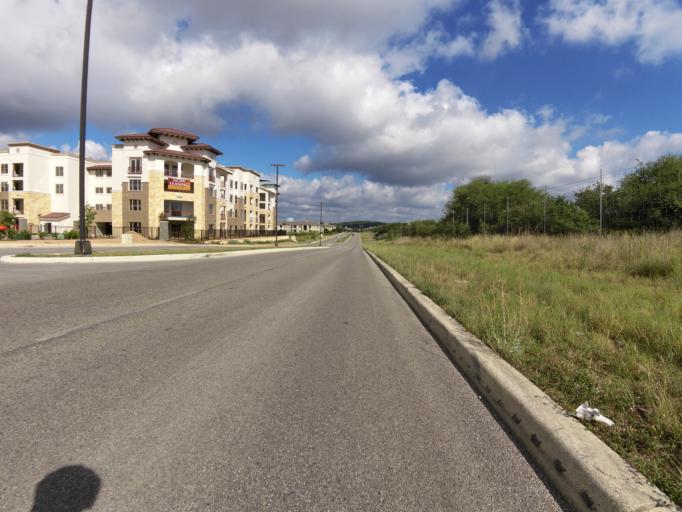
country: US
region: Texas
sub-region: Bexar County
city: Shavano Park
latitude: 29.5966
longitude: -98.5911
